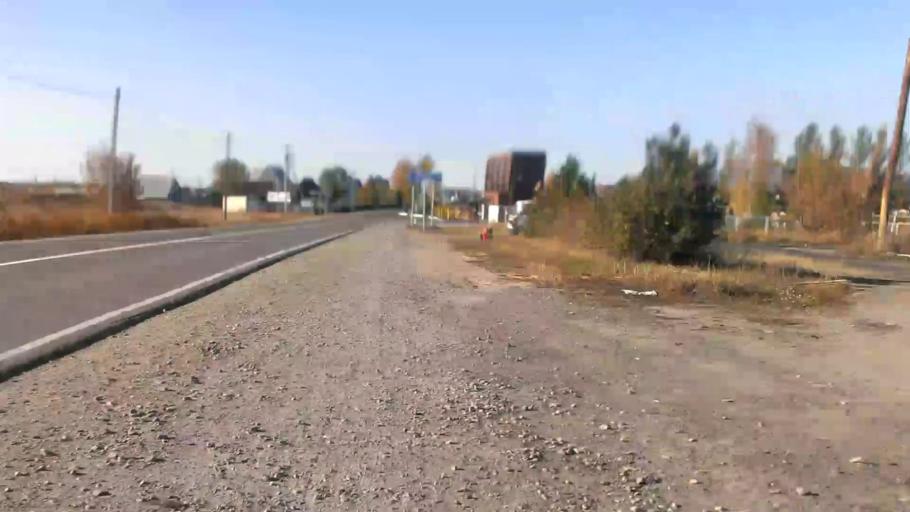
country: RU
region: Altai Krai
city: Sannikovo
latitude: 53.3132
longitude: 83.9632
